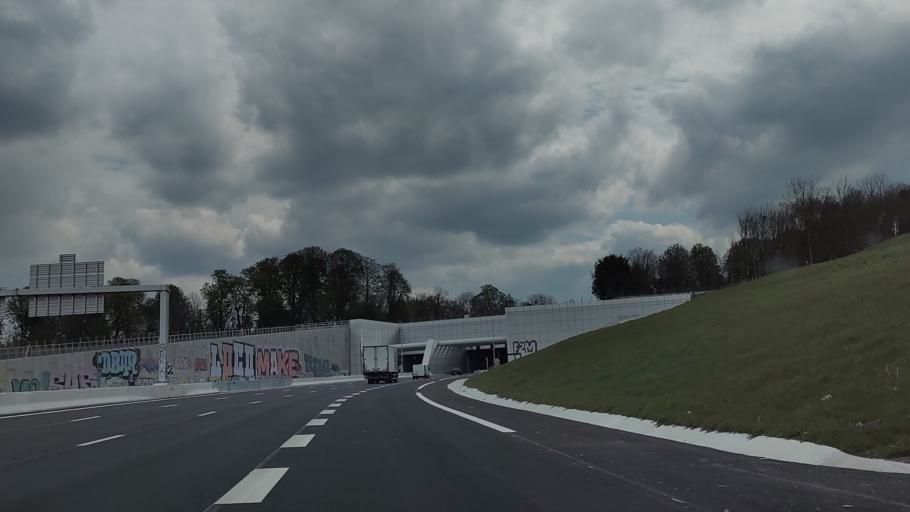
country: FR
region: Ile-de-France
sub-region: Departement du Val-de-Marne
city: Boissy-Saint-Leger
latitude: 48.7542
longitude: 2.5097
